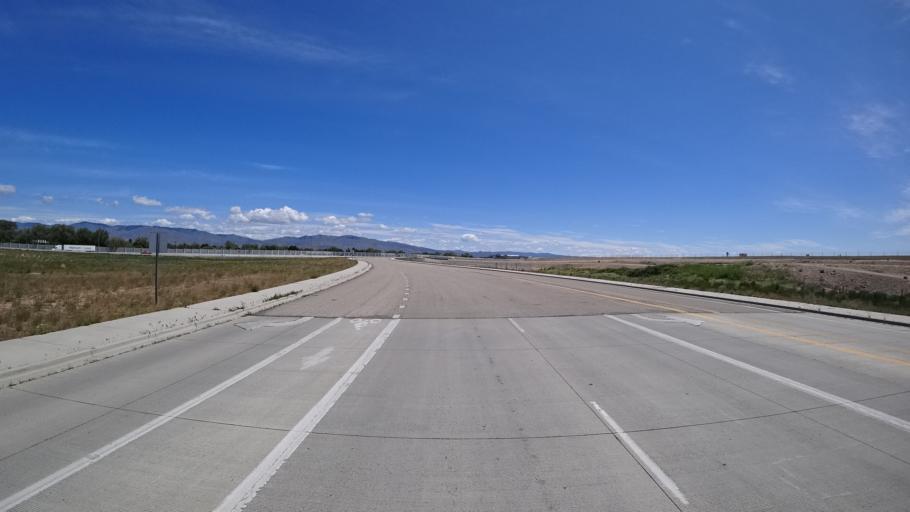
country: US
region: Idaho
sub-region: Ada County
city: Garden City
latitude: 43.5726
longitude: -116.2438
